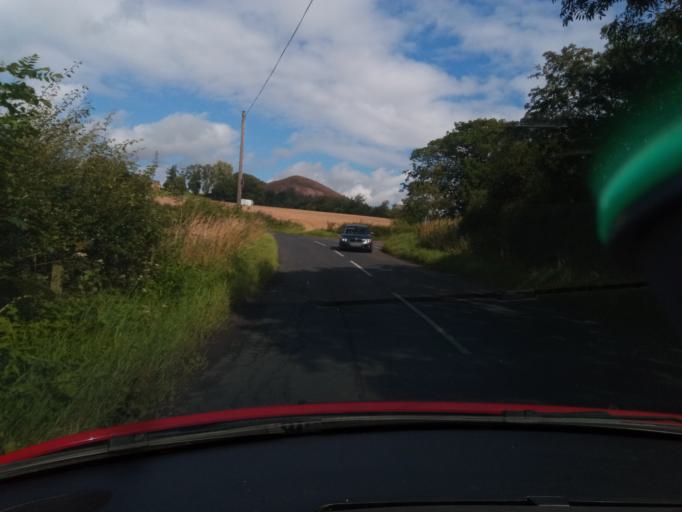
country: GB
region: Scotland
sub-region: The Scottish Borders
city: Melrose
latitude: 55.5620
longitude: -2.7190
